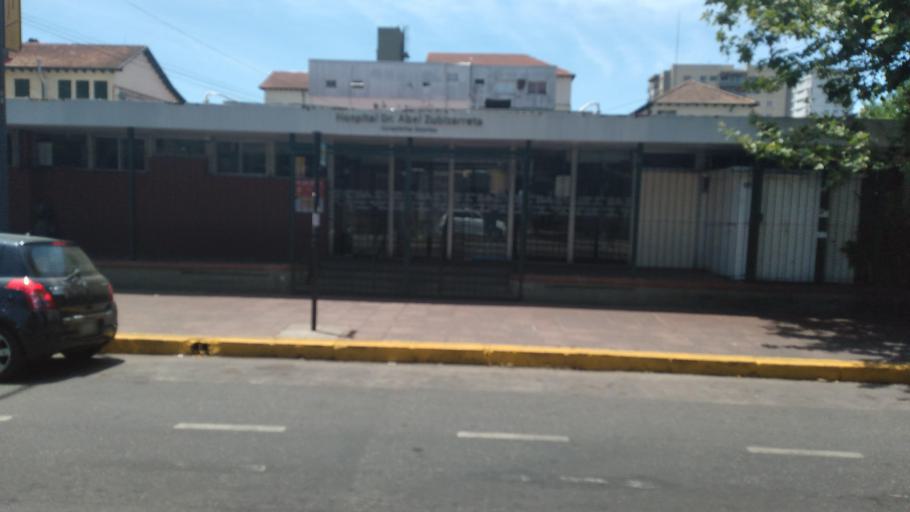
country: AR
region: Buenos Aires F.D.
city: Villa Santa Rita
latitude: -34.6006
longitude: -58.5112
